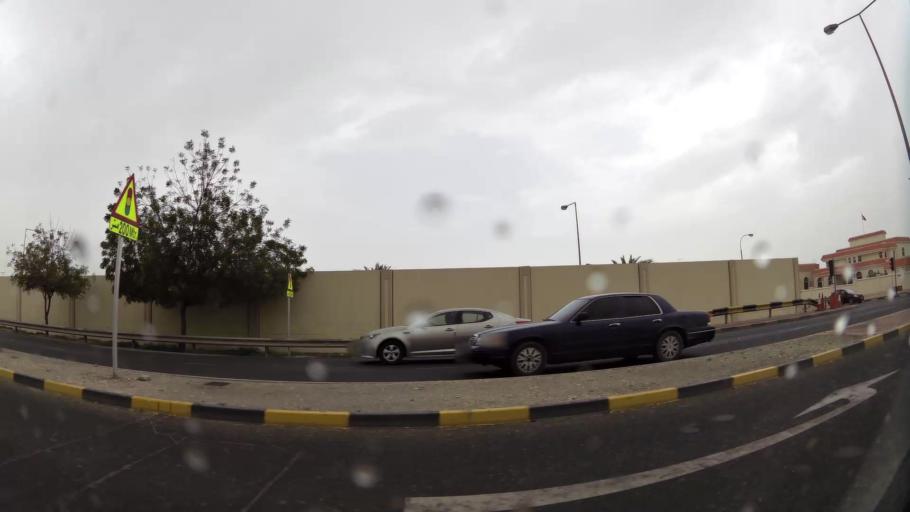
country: BH
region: Northern
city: Ar Rifa'
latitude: 26.1406
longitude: 50.5543
